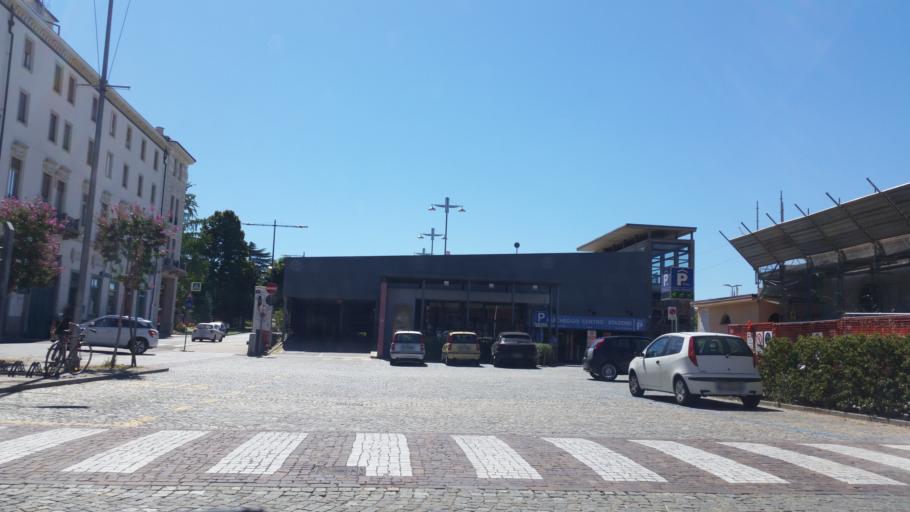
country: IT
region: Piedmont
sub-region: Provincia di Cuneo
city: Alba
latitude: 44.6980
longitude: 8.0310
